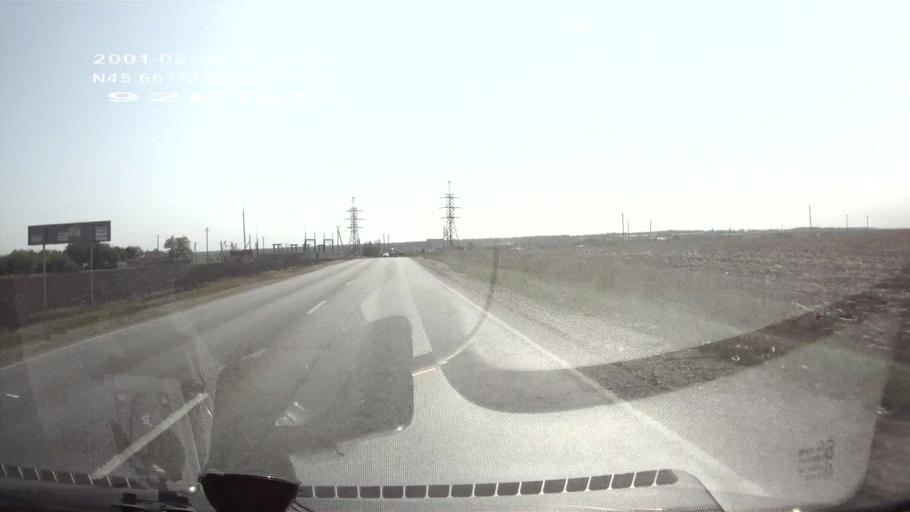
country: RU
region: Krasnodarskiy
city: Dmitriyevskaya
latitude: 45.6611
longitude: 40.7489
